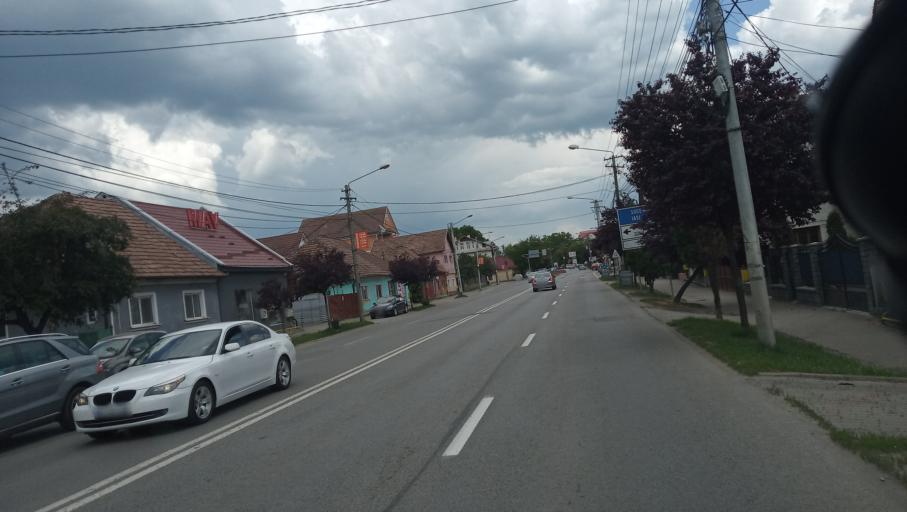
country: RO
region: Bistrita-Nasaud
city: Bistrita
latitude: 47.1224
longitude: 24.4759
